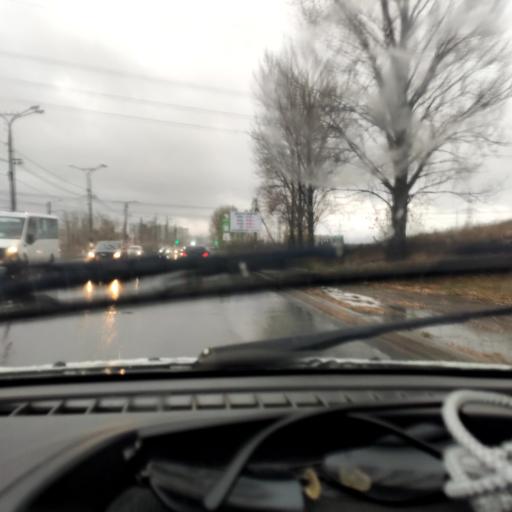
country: RU
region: Samara
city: Zhigulevsk
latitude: 53.4875
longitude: 49.5060
